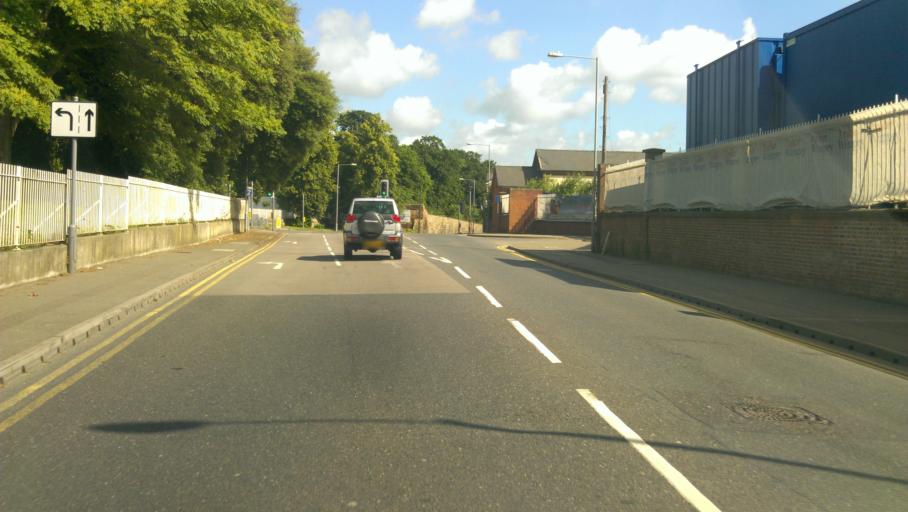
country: GB
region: England
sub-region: Essex
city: Colchester
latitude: 51.8824
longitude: 0.9034
